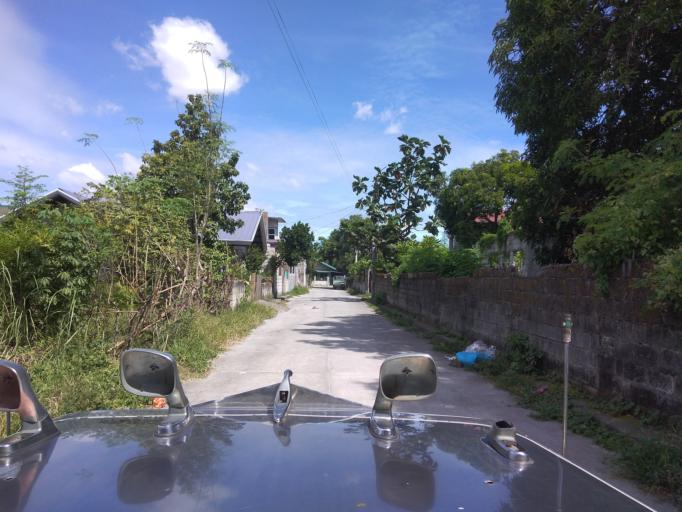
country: PH
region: Central Luzon
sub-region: Province of Pampanga
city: Magliman
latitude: 15.0385
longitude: 120.6540
